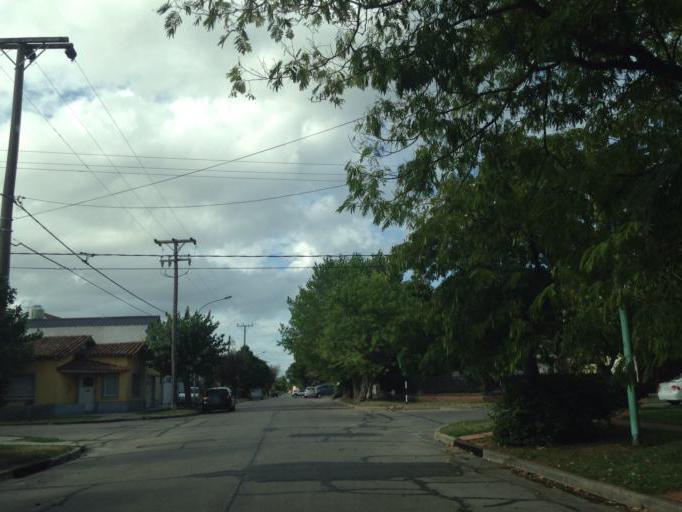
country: AR
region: Buenos Aires
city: Mar del Plata
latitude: -37.9768
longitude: -57.5611
